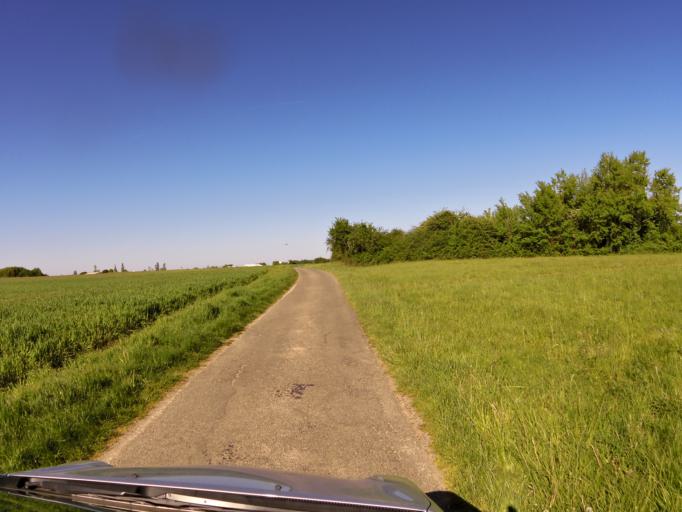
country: FR
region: Aquitaine
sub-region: Departement de la Dordogne
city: Domme
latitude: 44.7932
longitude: 1.2521
